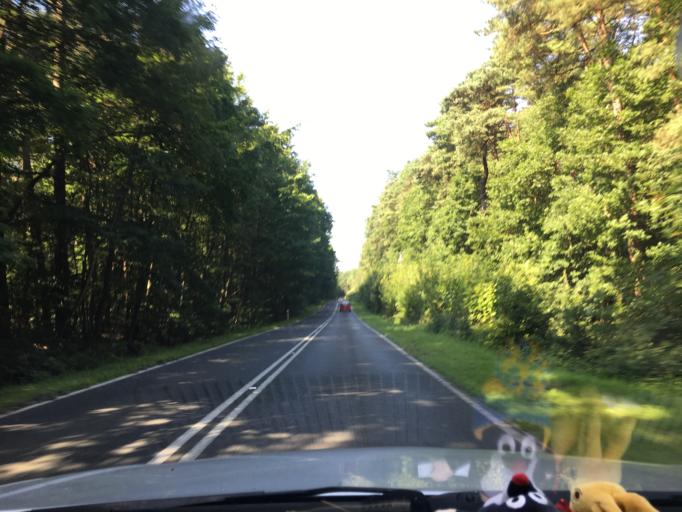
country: PL
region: West Pomeranian Voivodeship
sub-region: Powiat kamienski
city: Miedzyzdroje
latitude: 53.9663
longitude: 14.5561
